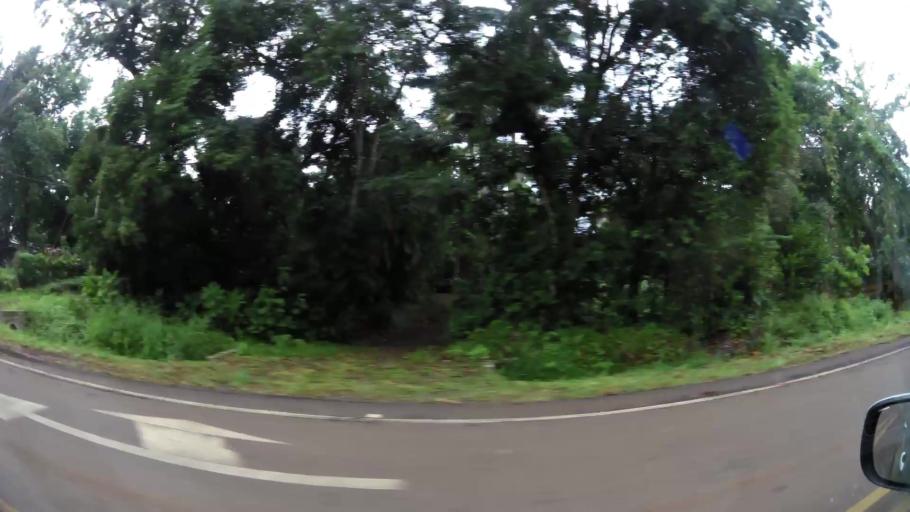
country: CR
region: Puntarenas
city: Esparza
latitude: 9.9601
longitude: -84.5979
